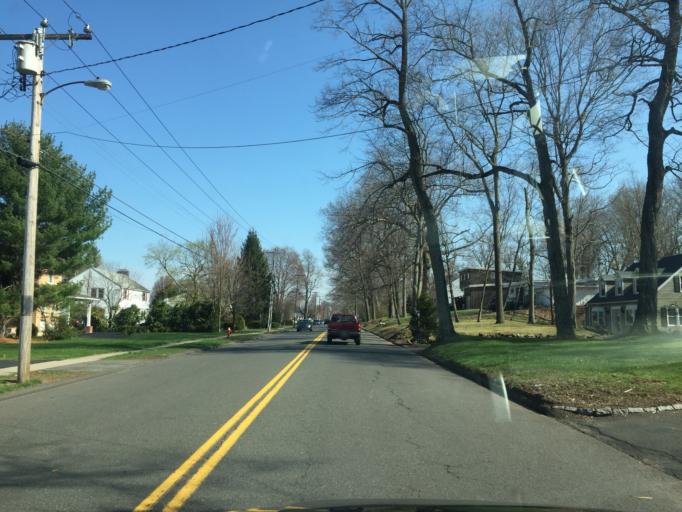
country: US
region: Connecticut
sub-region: Hartford County
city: Wethersfield
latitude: 41.6989
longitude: -72.6848
